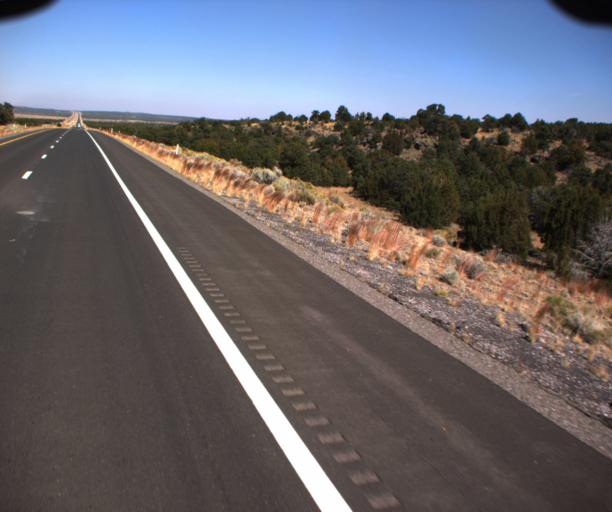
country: US
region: Arizona
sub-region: Coconino County
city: Flagstaff
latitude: 35.4169
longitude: -111.5716
